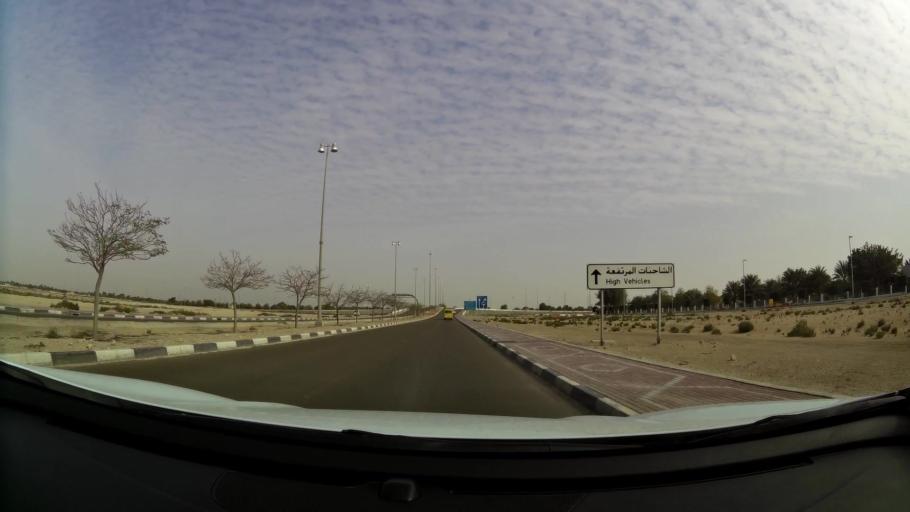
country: AE
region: Abu Dhabi
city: Abu Dhabi
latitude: 24.6231
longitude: 54.7120
